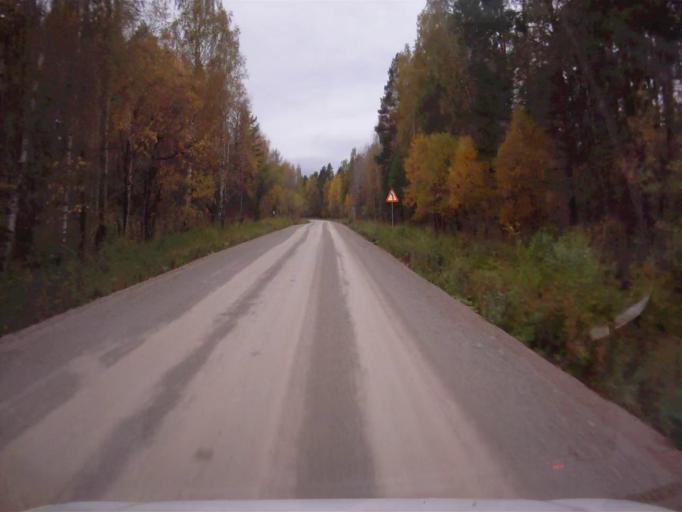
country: RU
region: Chelyabinsk
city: Nyazepetrovsk
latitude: 56.0645
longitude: 59.4416
